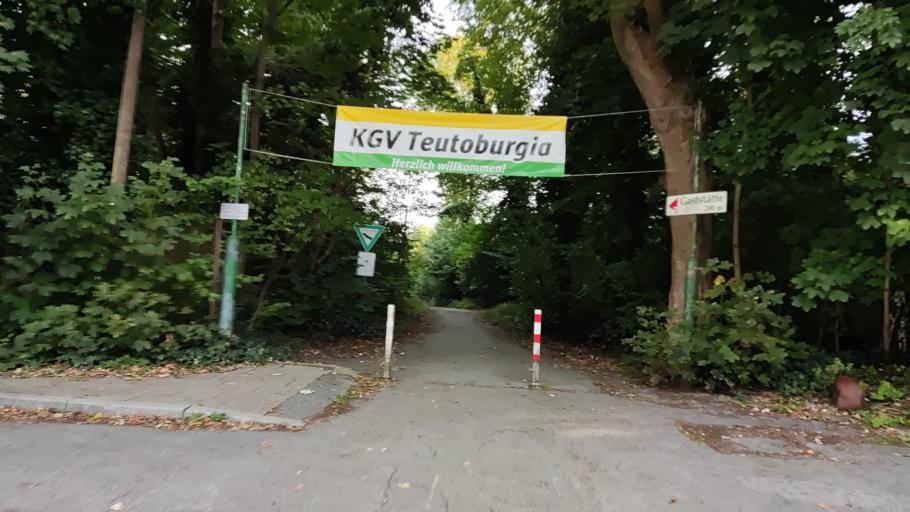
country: DE
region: North Rhine-Westphalia
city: Castrop-Rauxel
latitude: 51.5531
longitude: 7.2756
